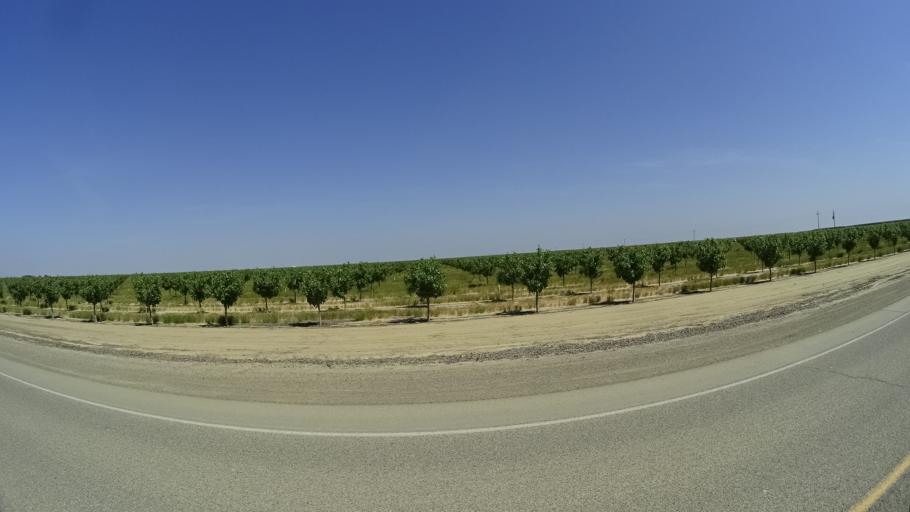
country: US
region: California
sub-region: Fresno County
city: Huron
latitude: 36.1378
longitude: -120.0151
